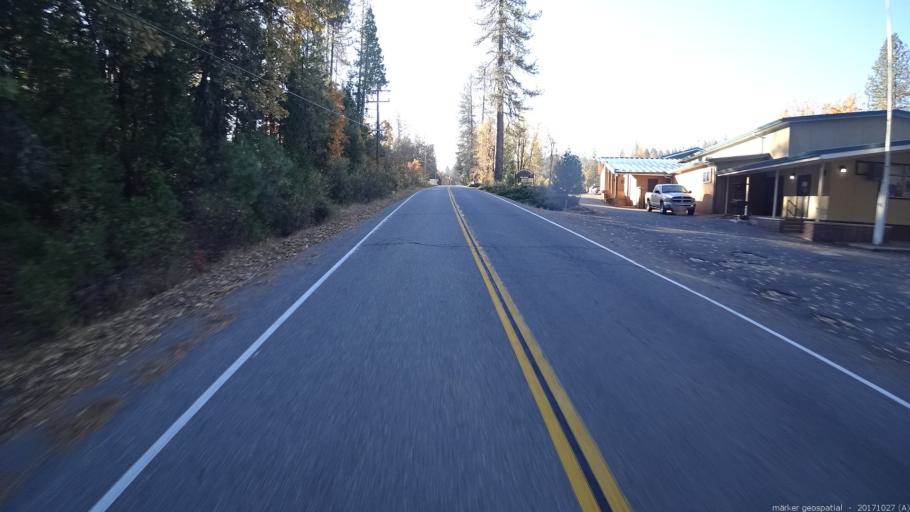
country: US
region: California
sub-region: Shasta County
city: Burney
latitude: 41.0162
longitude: -121.9068
